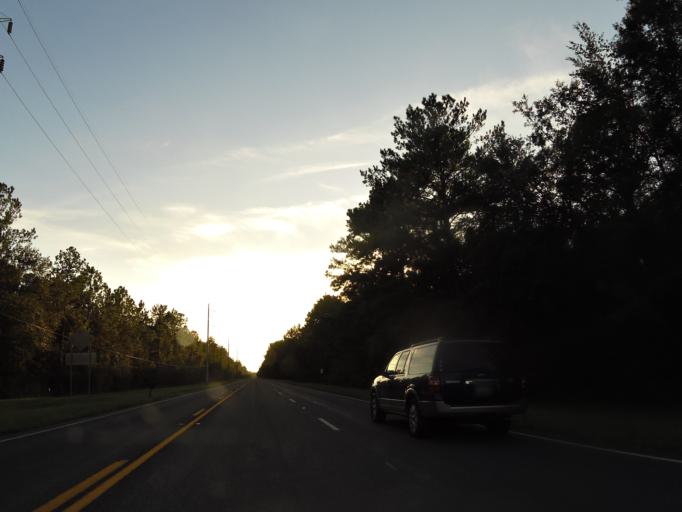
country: US
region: Georgia
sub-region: Camden County
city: Woodbine
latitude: 31.1045
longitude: -81.6853
